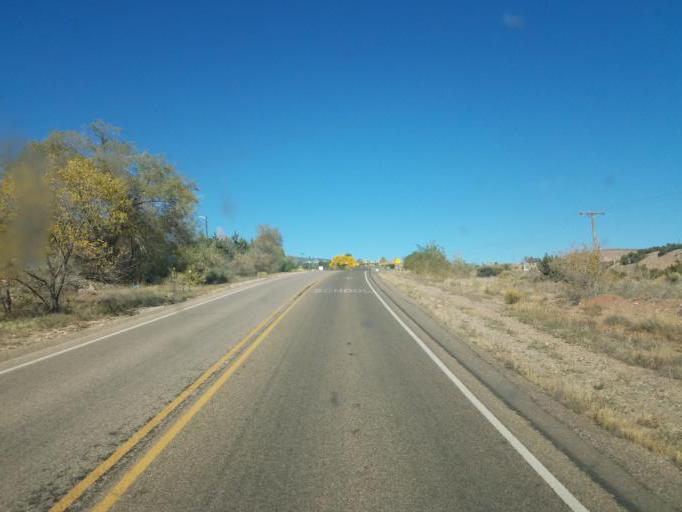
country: US
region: New Mexico
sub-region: Sandoval County
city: Jemez Pueblo
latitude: 35.6548
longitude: -106.7346
